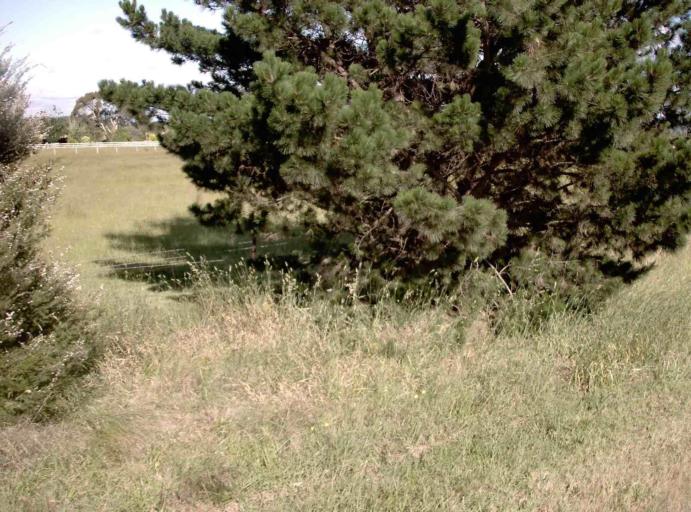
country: AU
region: Victoria
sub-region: Latrobe
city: Traralgon
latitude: -38.1867
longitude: 146.5032
